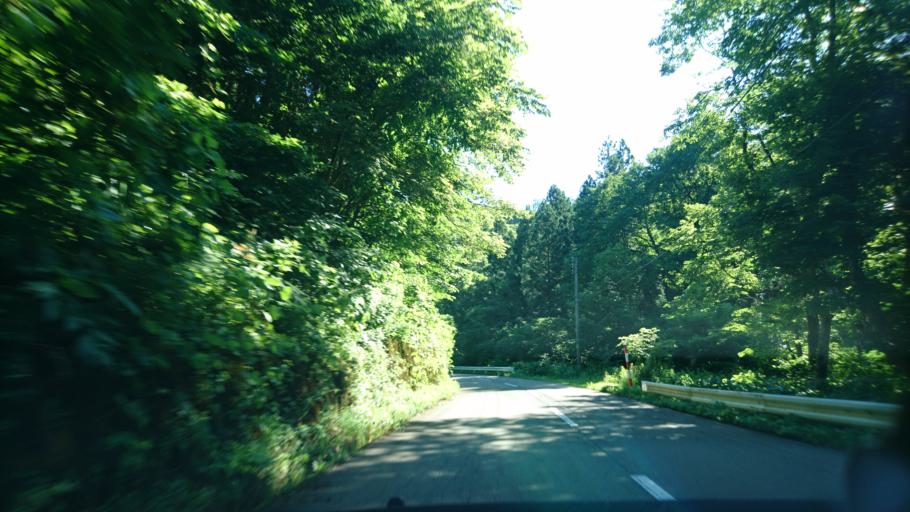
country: JP
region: Akita
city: Kakunodatemachi
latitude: 39.7118
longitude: 140.6172
